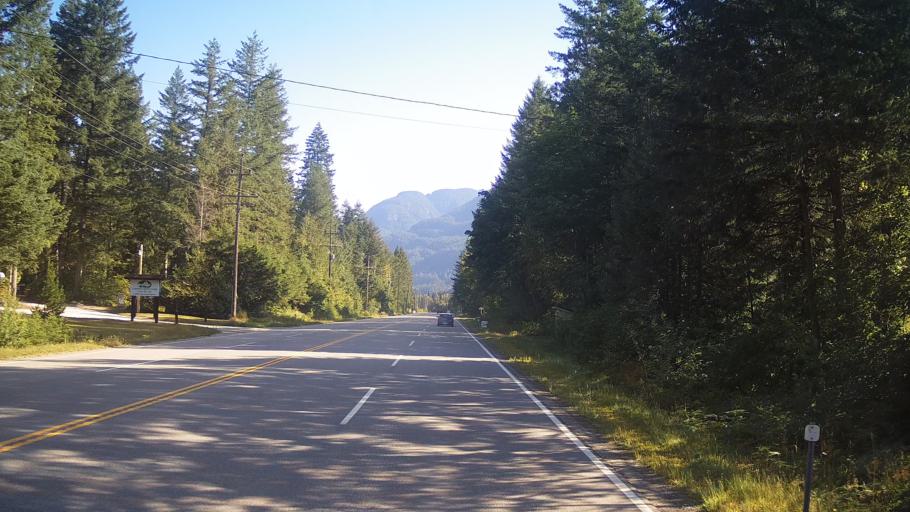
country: CA
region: British Columbia
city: Hope
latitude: 49.4711
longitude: -121.4284
